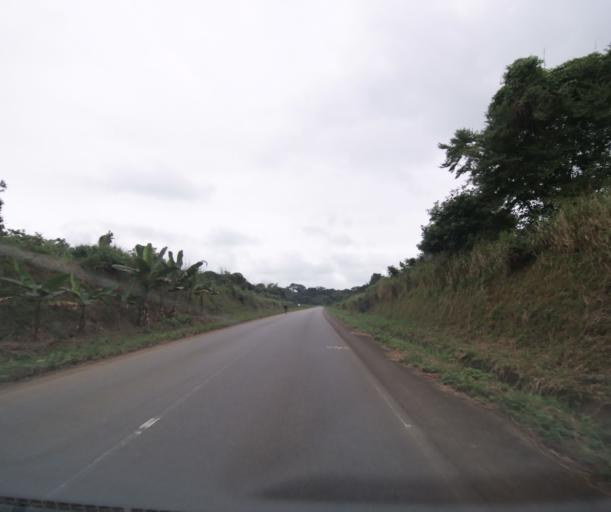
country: CM
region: Littoral
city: Edea
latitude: 3.7253
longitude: 10.1102
